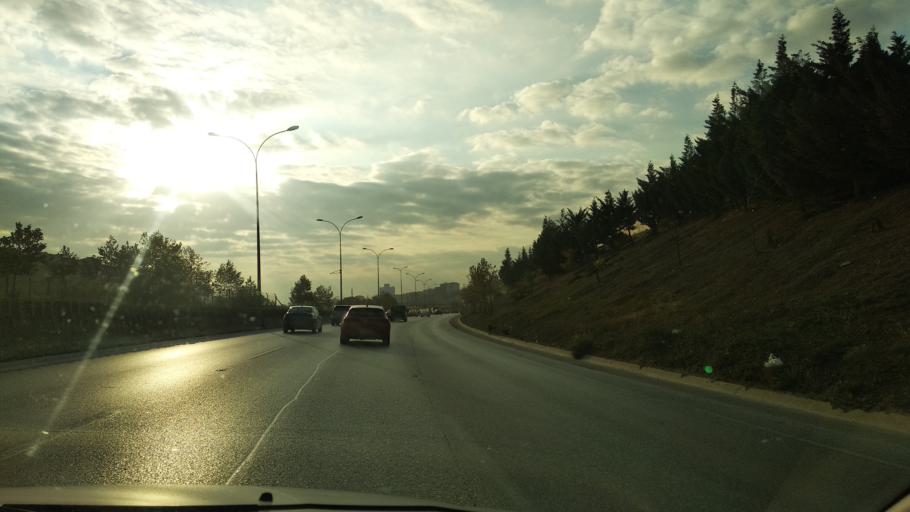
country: TR
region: Istanbul
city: Pendik
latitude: 40.8748
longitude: 29.2999
